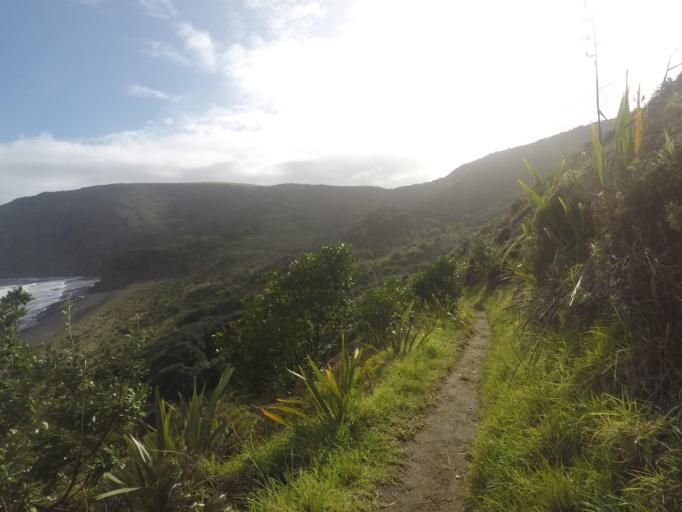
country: NZ
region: Auckland
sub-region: Auckland
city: Muriwai Beach
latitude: -36.8856
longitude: 174.4398
